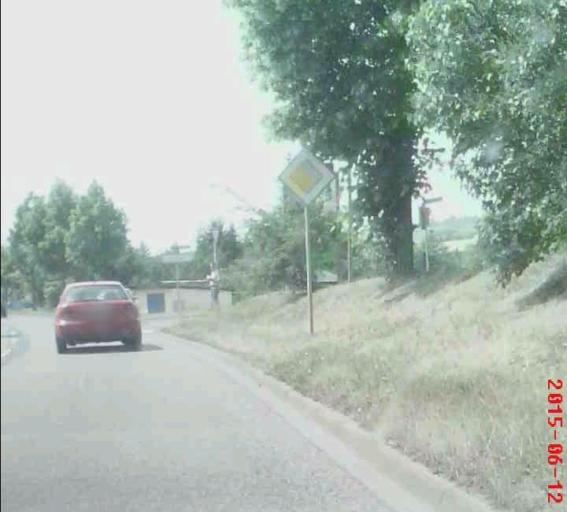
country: DE
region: Saxony-Anhalt
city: Sangerhausen
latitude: 51.4689
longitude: 11.2774
